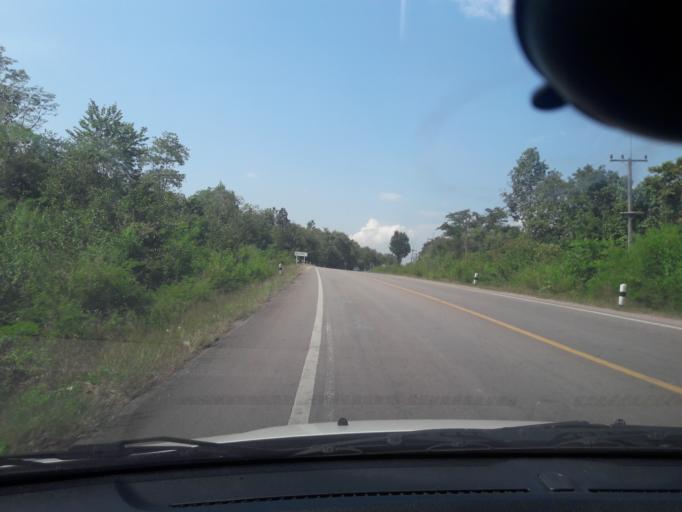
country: TH
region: Lampang
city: Mae Tha
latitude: 18.1886
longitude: 99.5348
